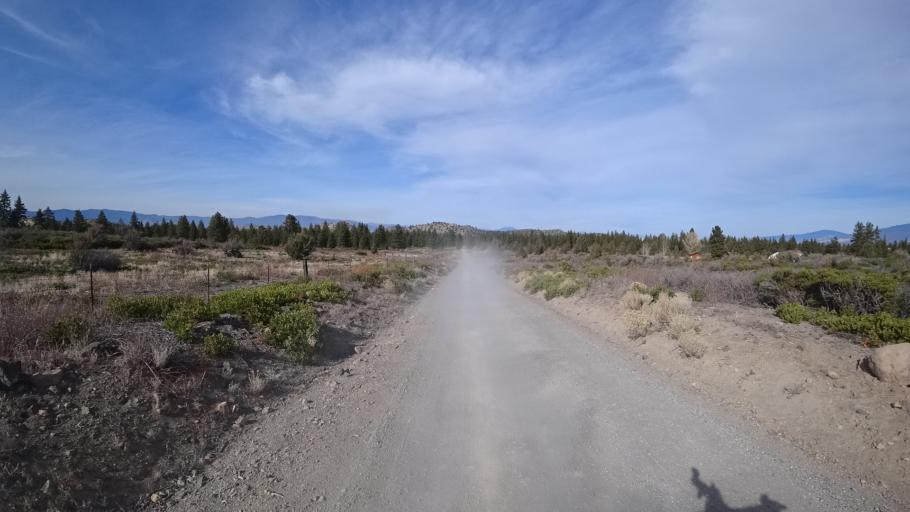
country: US
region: California
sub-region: Siskiyou County
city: Weed
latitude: 41.4876
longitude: -122.3689
